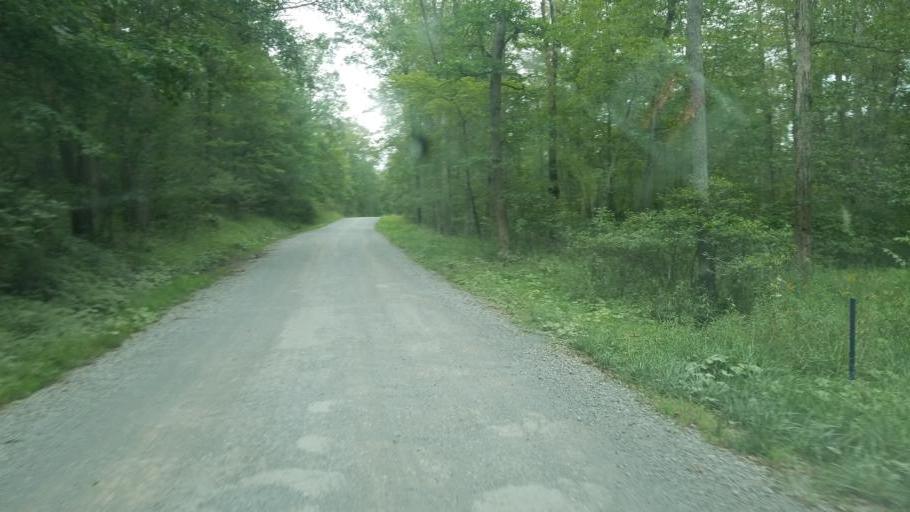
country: US
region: Pennsylvania
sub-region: Clarion County
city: Clarion
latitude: 41.2259
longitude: -79.4082
